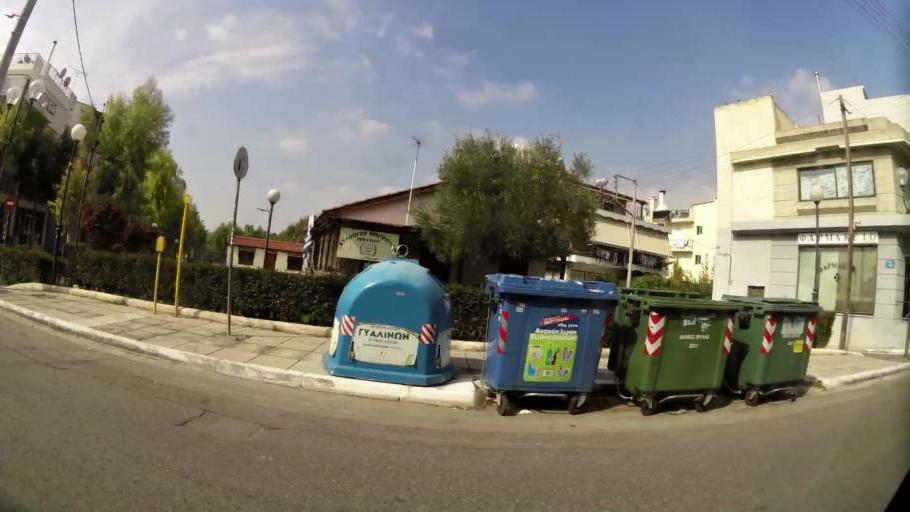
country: GR
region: Attica
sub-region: Nomarchia Dytikis Attikis
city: Zefyri
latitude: 38.0688
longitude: 23.7162
